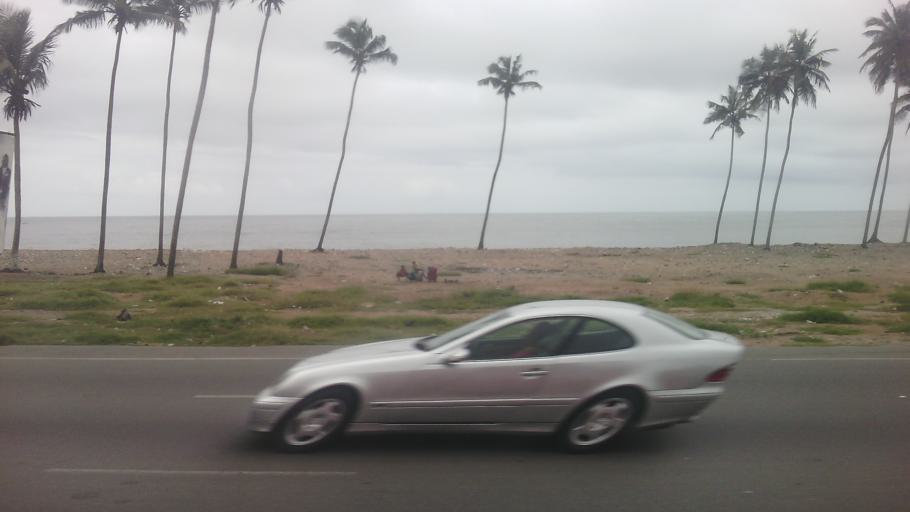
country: CI
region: Lagunes
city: Abidjan
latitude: 5.2461
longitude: -3.9392
